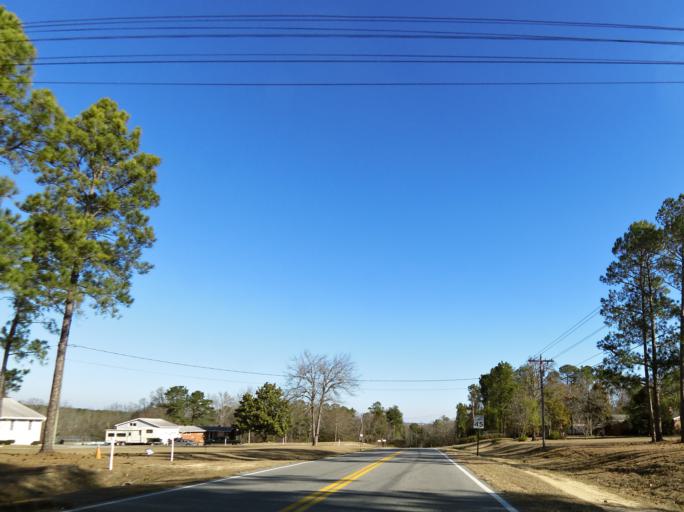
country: US
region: Georgia
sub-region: Bibb County
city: West Point
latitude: 32.7595
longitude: -83.7608
